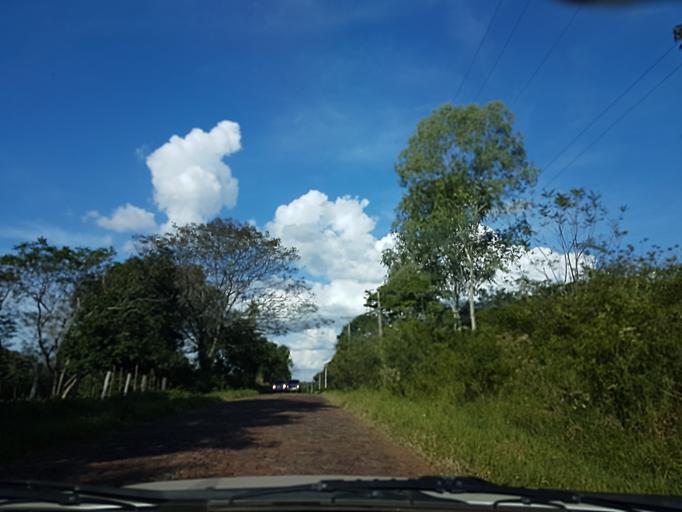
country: PY
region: Cordillera
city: Arroyos y Esteros
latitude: -24.9975
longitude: -57.1804
